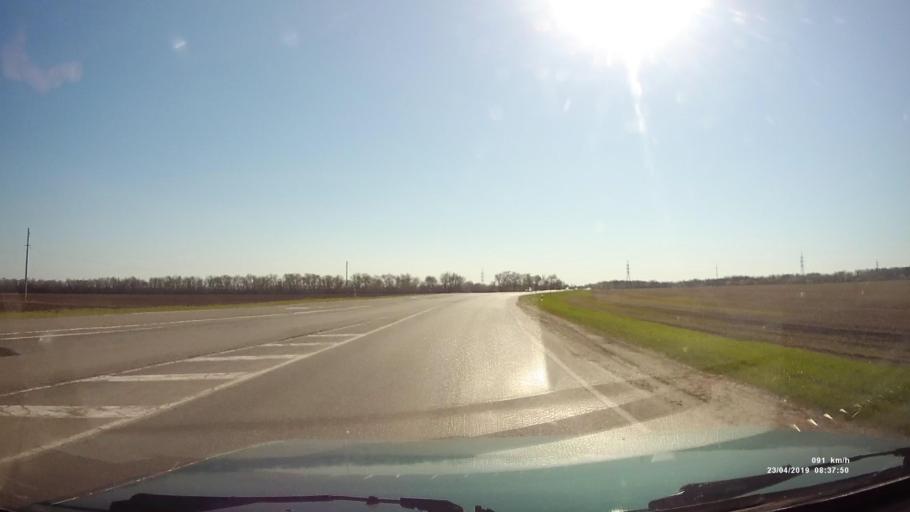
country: RU
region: Rostov
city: Tselina
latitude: 46.5324
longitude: 41.1758
